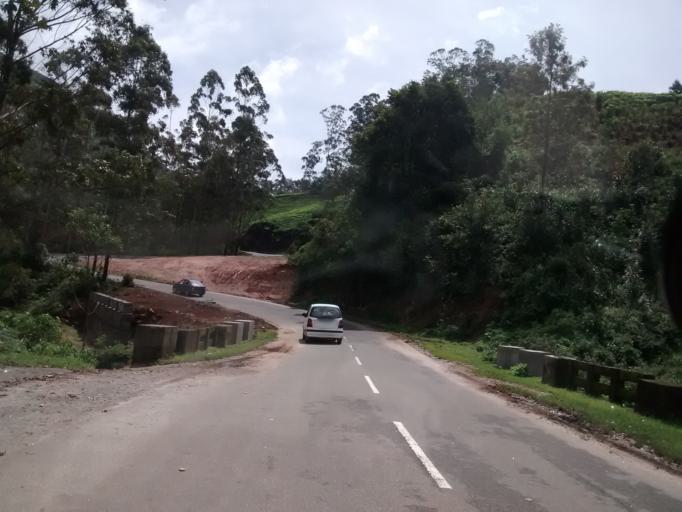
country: IN
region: Kerala
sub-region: Idukki
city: Munnar
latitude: 10.0895
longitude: 77.0855
